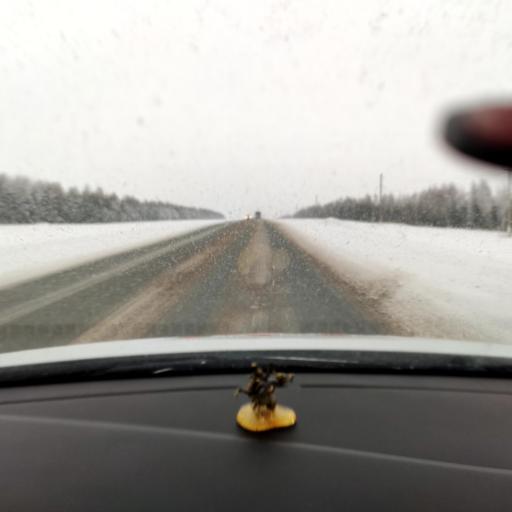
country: RU
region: Tatarstan
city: Vysokaya Gora
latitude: 56.0203
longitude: 49.2623
